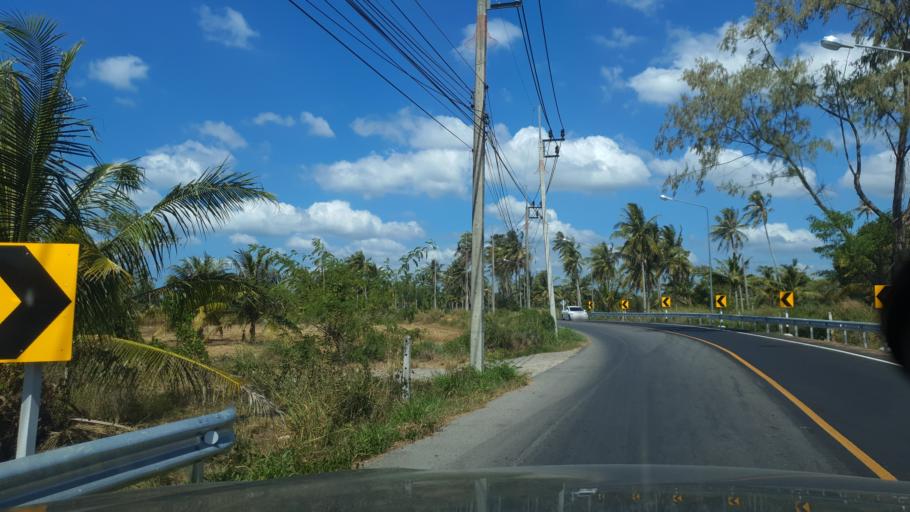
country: TH
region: Phuket
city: Thalang
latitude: 8.1449
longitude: 98.3059
